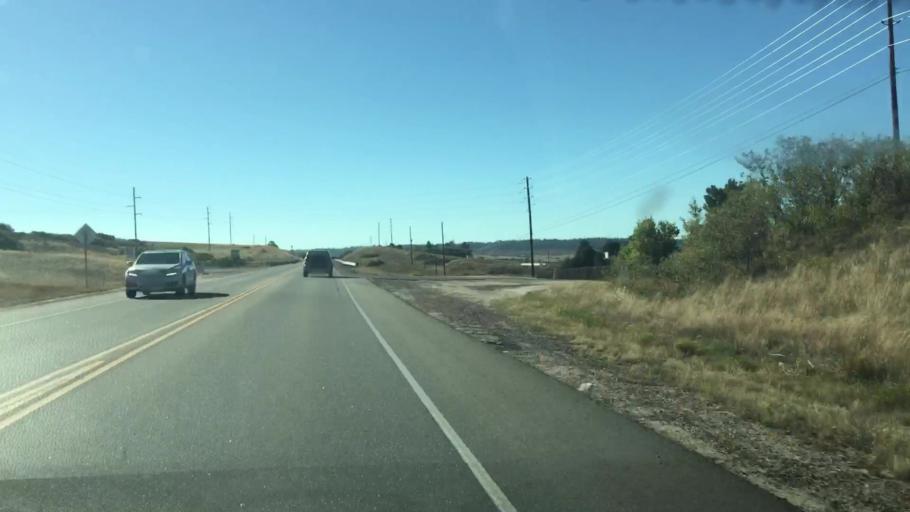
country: US
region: Colorado
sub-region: Douglas County
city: The Pinery
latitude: 39.4040
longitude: -104.7583
